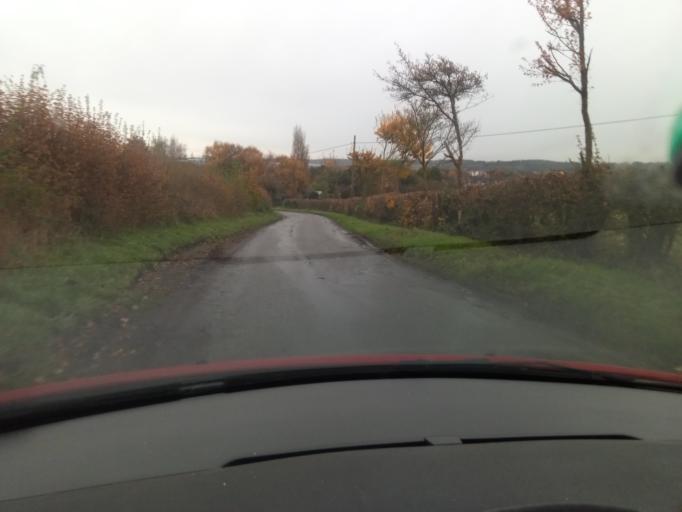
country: GB
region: England
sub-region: Derbyshire
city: Borrowash
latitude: 52.8638
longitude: -1.3965
